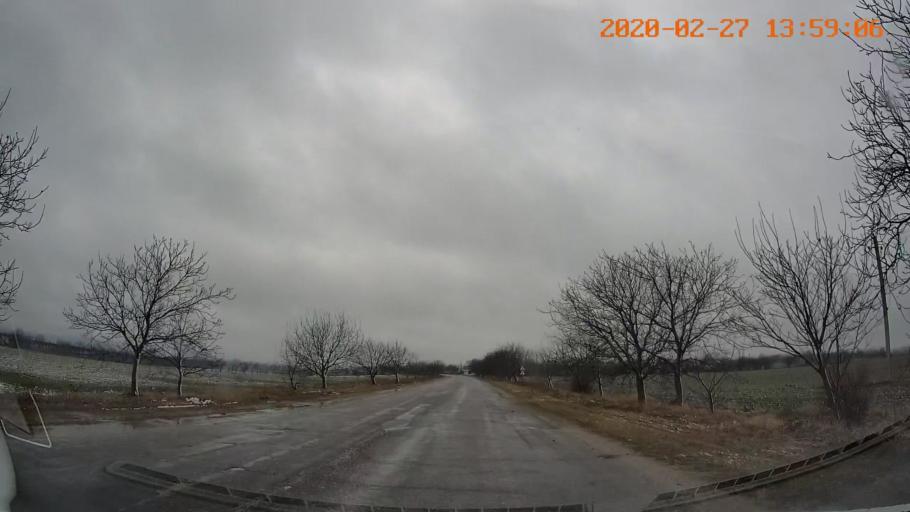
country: MD
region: Singerei
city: Bilicenii Vechi
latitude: 47.6036
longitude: 28.0249
